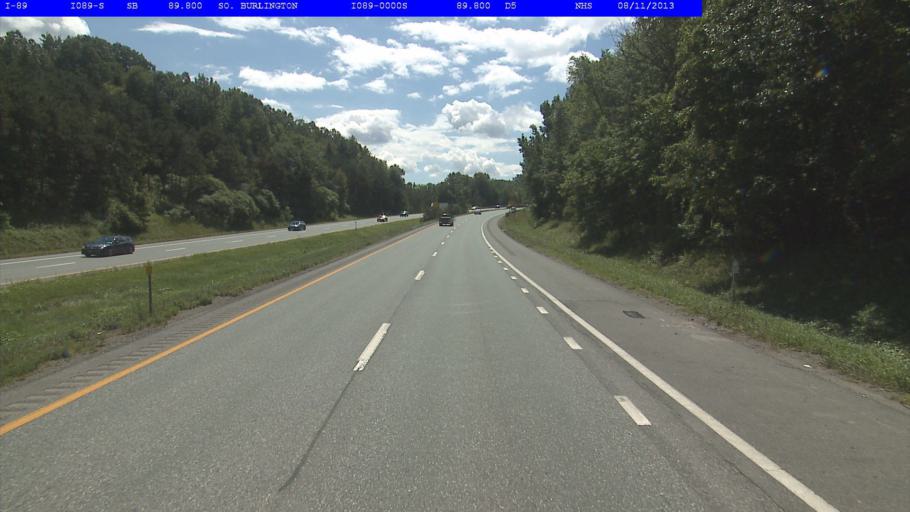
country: US
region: Vermont
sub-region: Chittenden County
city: Winooski
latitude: 44.4835
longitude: -73.1743
